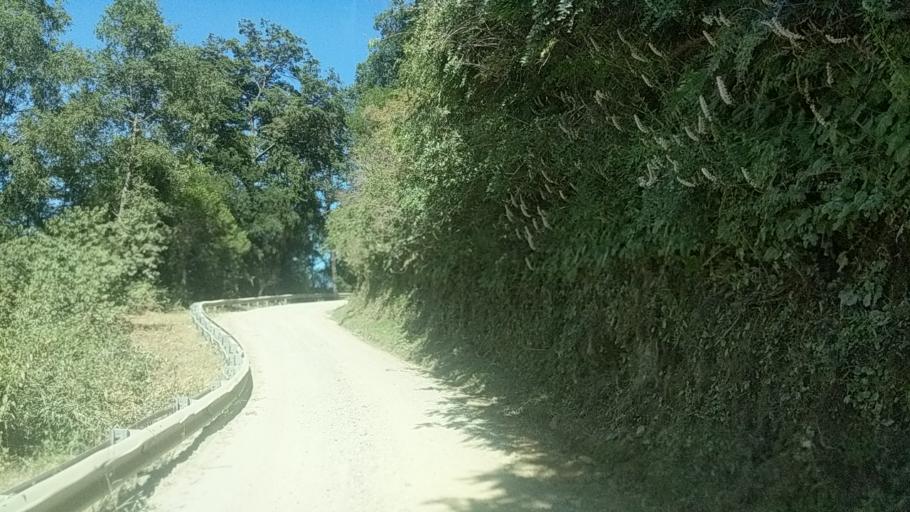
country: CL
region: Araucania
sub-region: Provincia de Cautin
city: Pucon
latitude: -39.0635
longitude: -71.7121
